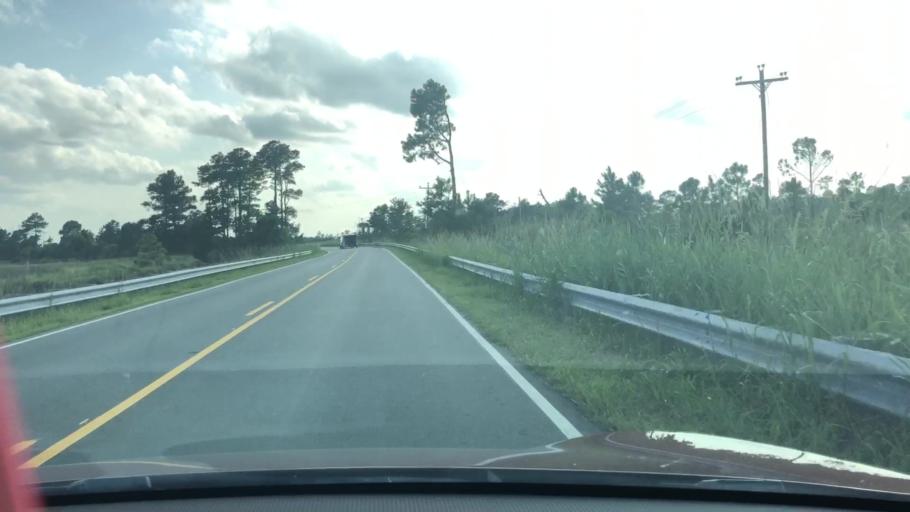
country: US
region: North Carolina
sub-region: Dare County
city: Wanchese
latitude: 35.6939
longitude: -75.7782
